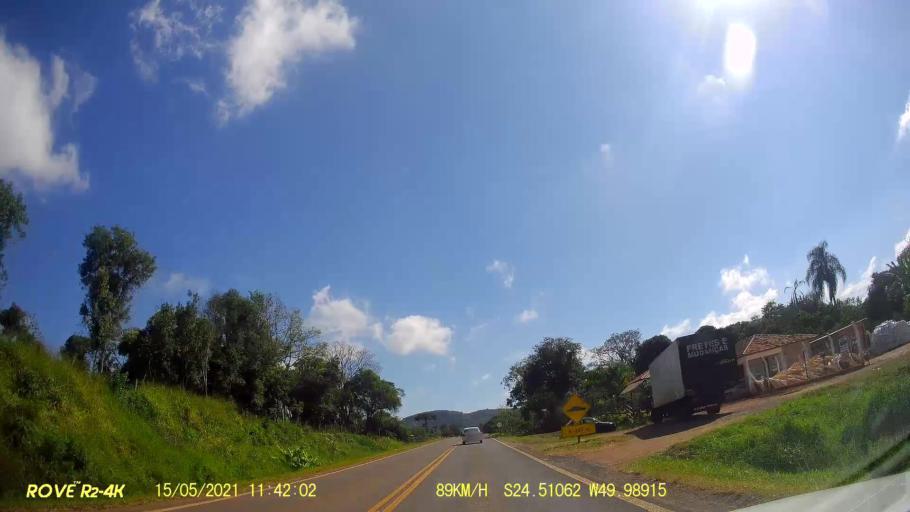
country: BR
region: Parana
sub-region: Pirai Do Sul
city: Pirai do Sul
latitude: -24.5107
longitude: -49.9891
